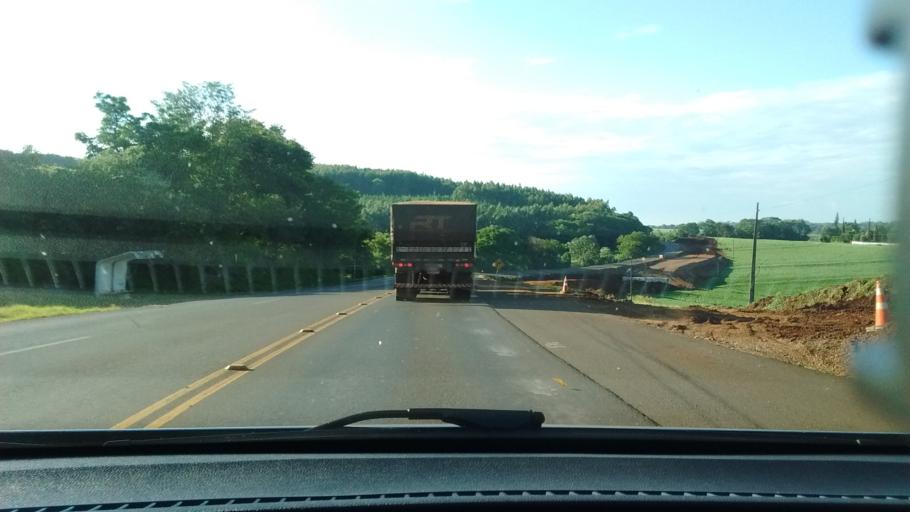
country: BR
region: Parana
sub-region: Cascavel
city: Cascavel
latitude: -25.2039
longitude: -53.5975
